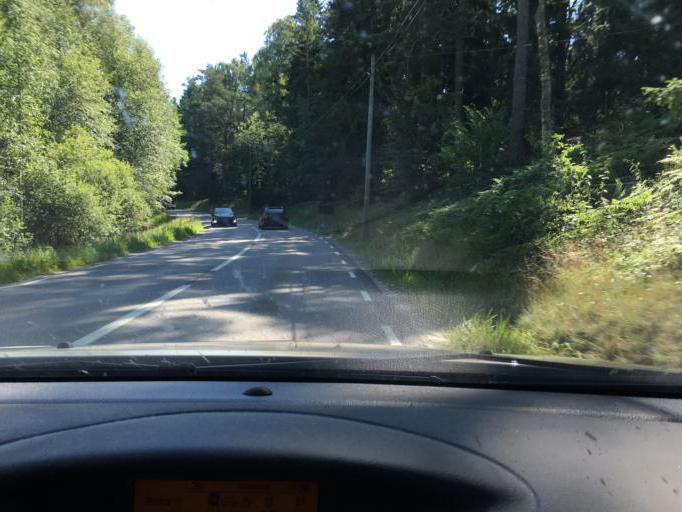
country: SE
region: Stockholm
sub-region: Varmdo Kommun
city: Mortnas
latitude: 59.2786
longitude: 18.4423
